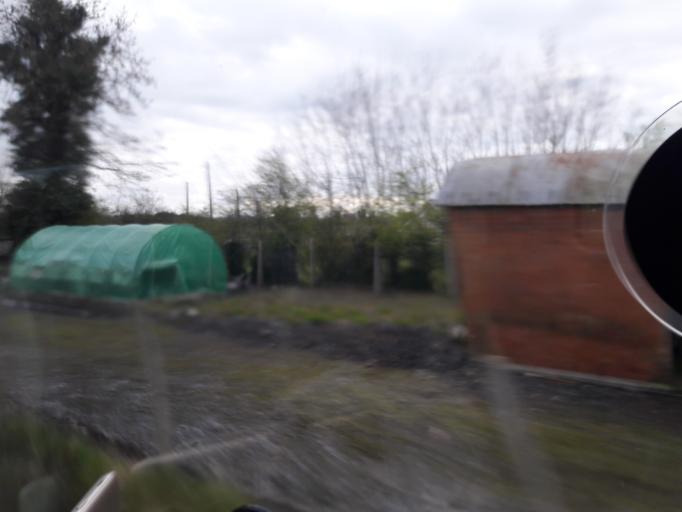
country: IE
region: Leinster
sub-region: An Longfort
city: Granard
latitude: 53.6699
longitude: -7.5000
